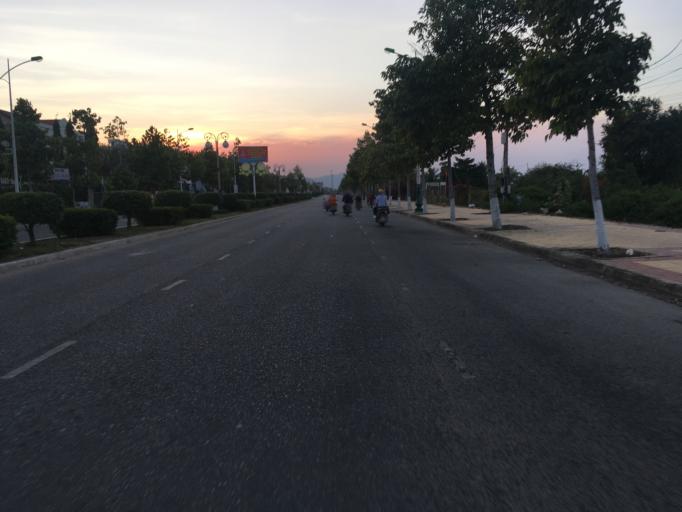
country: VN
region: Ninh Thuan
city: Phan Rang-Thap Cham
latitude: 11.5645
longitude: 109.0079
